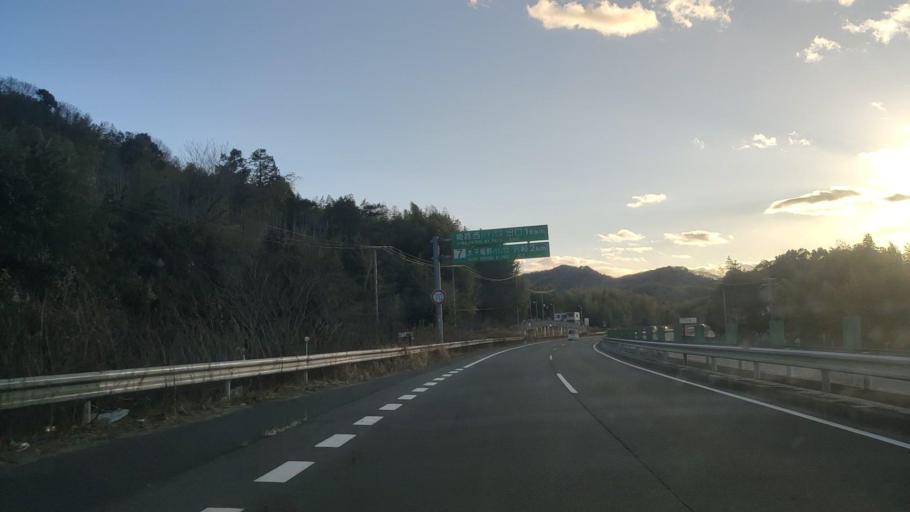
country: JP
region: Hyogo
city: Tatsunocho-tominaga
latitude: 34.8625
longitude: 134.6181
